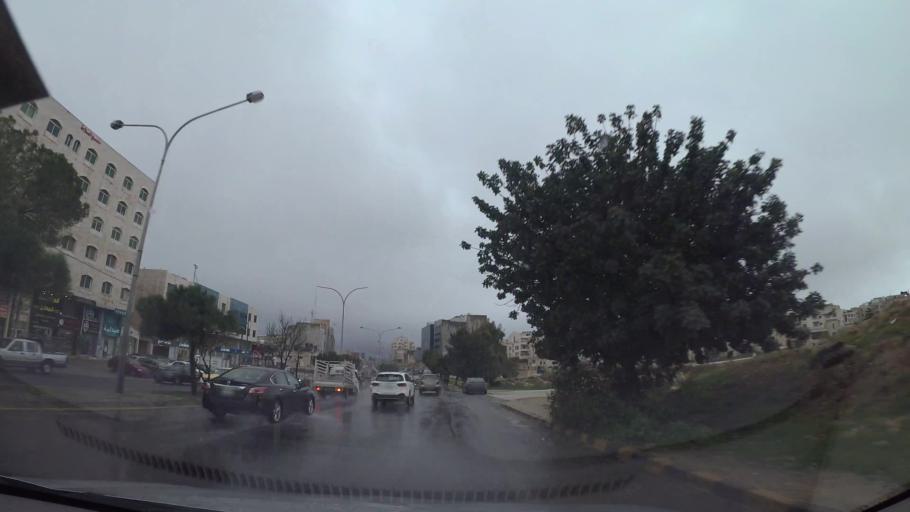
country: JO
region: Amman
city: Al Jubayhah
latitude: 32.0279
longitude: 35.8591
